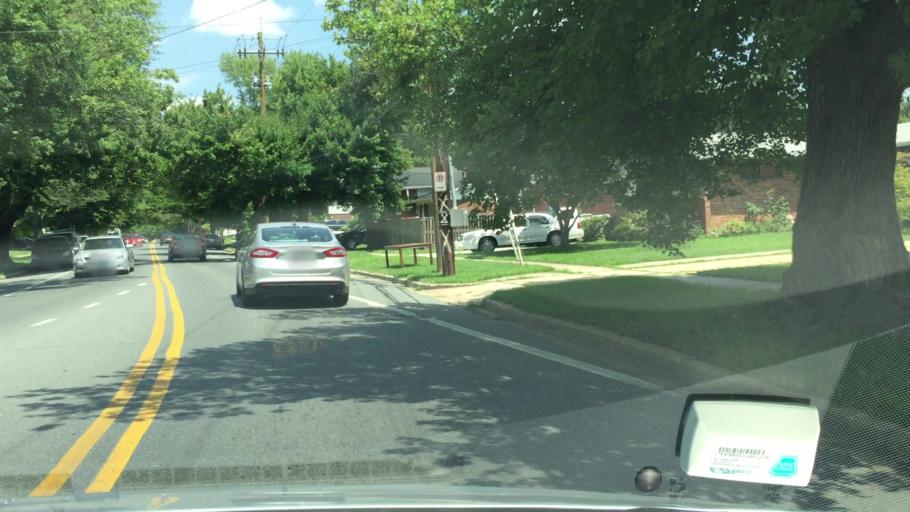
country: US
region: Maryland
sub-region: Montgomery County
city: Aspen Hill
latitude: 39.0714
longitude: -77.0985
